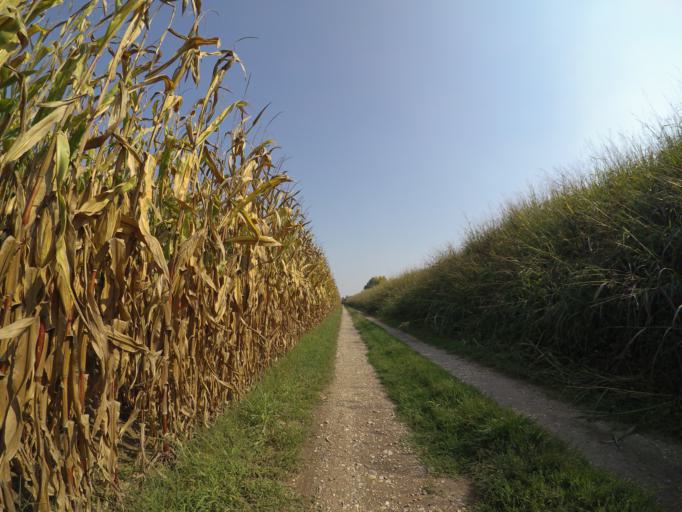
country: IT
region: Friuli Venezia Giulia
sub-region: Provincia di Udine
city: Varmo
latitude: 45.8836
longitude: 12.9719
